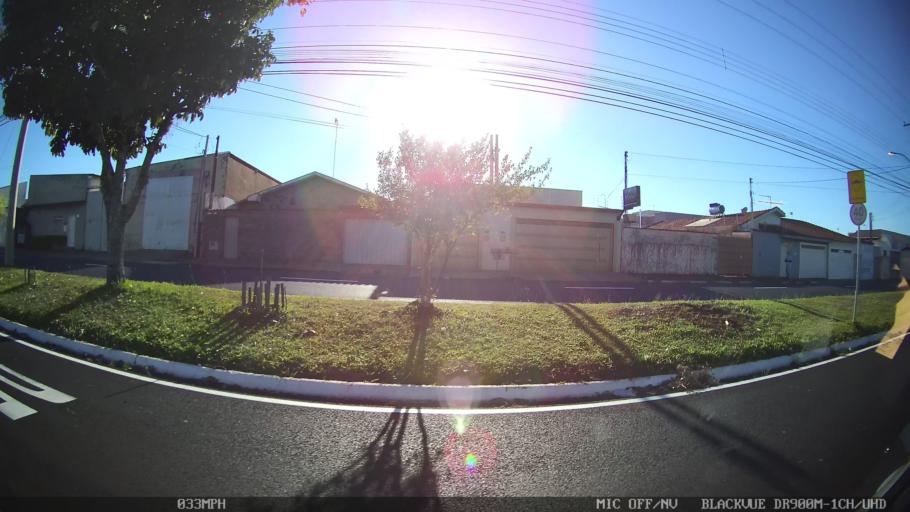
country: BR
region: Sao Paulo
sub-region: Franca
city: Franca
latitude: -20.5657
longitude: -47.3971
